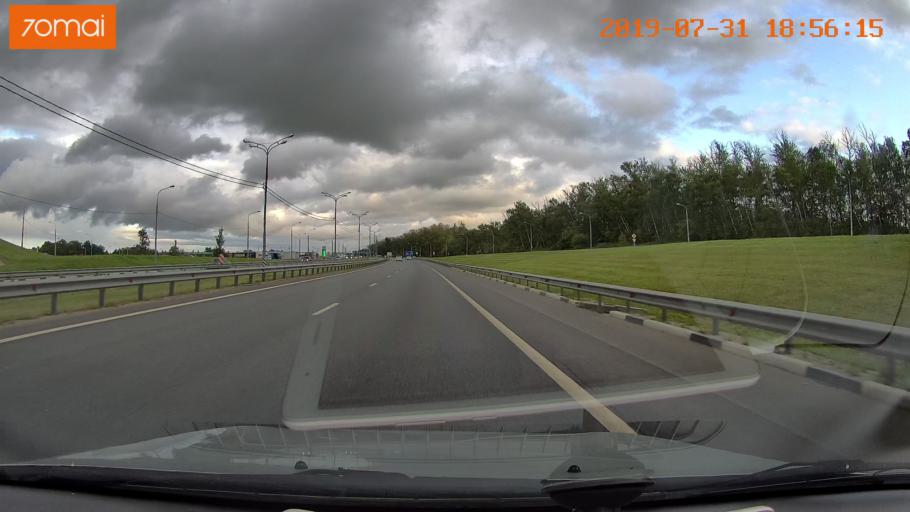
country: RU
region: Moskovskaya
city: Raduzhnyy
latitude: 55.1653
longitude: 38.6751
